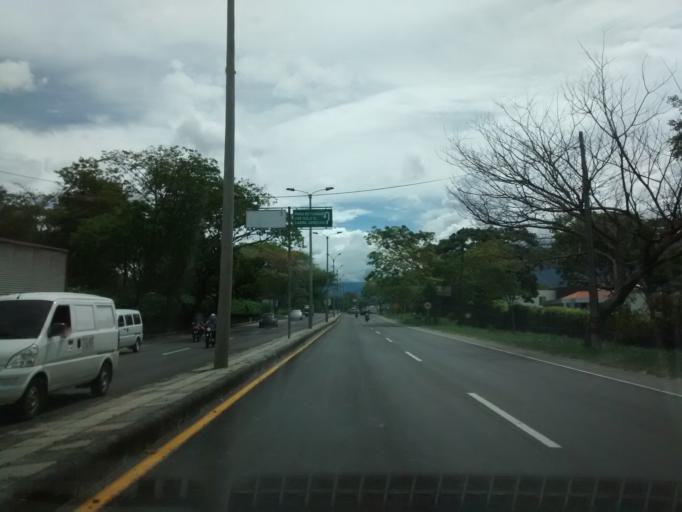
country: CO
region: Tolima
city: Ibague
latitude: 4.4049
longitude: -75.1626
